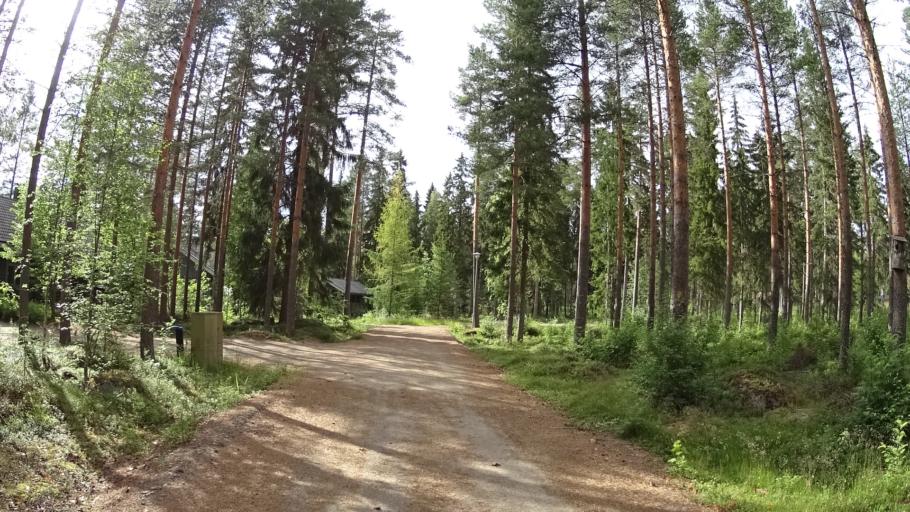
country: FI
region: Southern Ostrobothnia
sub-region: Kuusiokunnat
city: AEhtaeri
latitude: 62.5280
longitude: 24.1944
